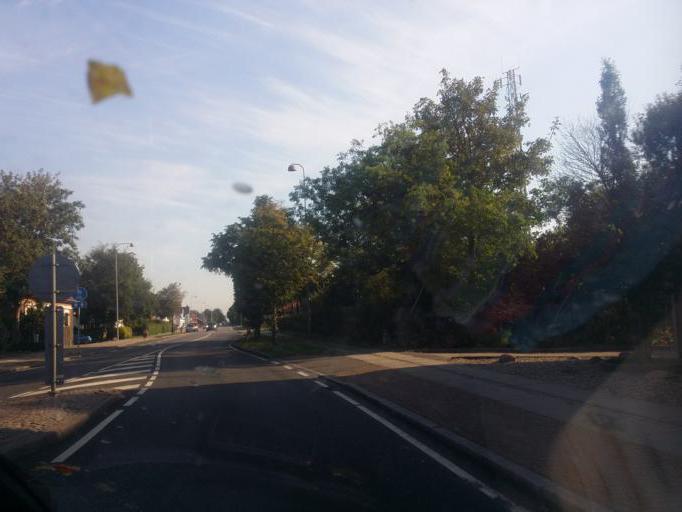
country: DK
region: South Denmark
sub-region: Esbjerg Kommune
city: Ribe
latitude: 55.2741
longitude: 8.7282
